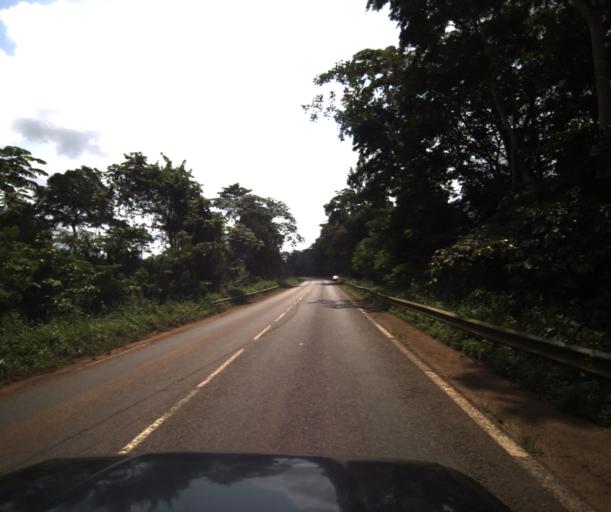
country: CM
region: Centre
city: Eseka
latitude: 3.8908
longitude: 10.7829
